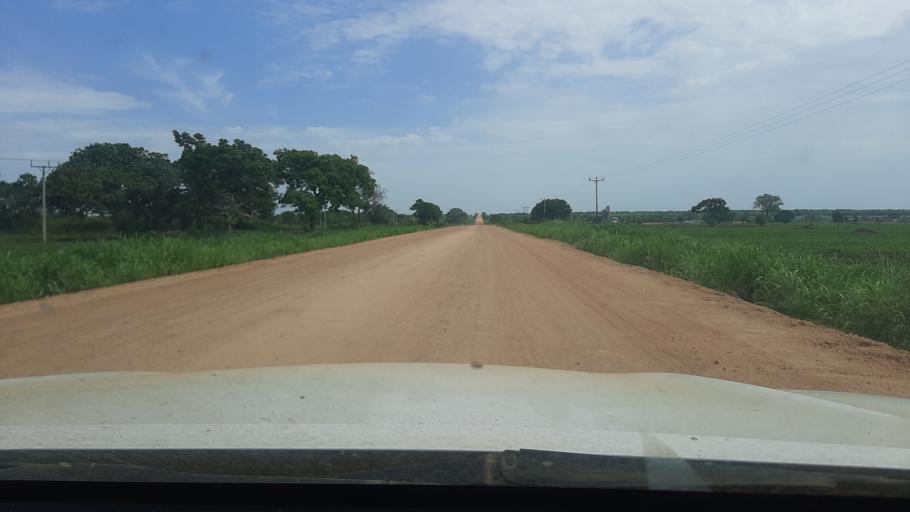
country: ET
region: Gambela
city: Gambela
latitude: 8.0289
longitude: 34.5758
